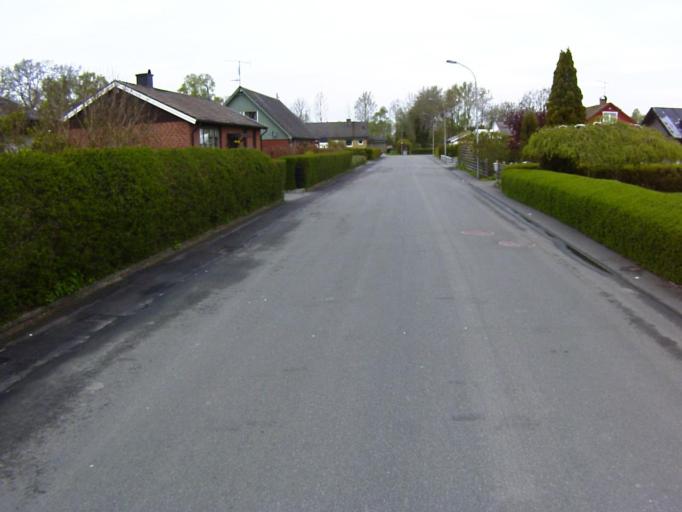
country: SE
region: Skane
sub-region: Kristianstads Kommun
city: Onnestad
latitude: 55.9360
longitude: 13.9692
